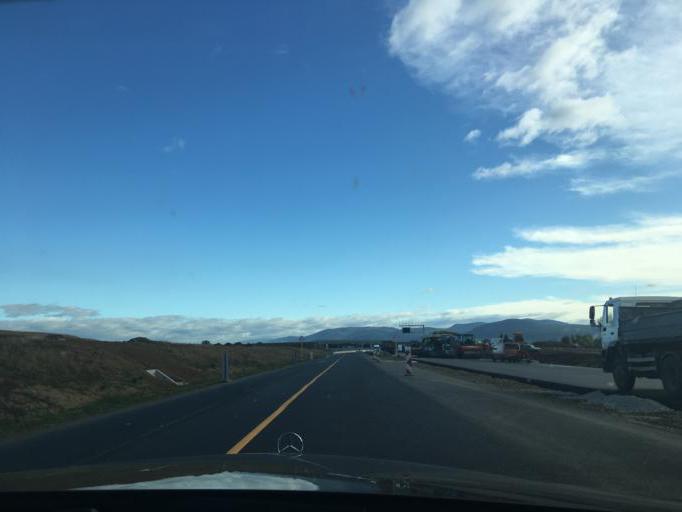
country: HU
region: Borsod-Abauj-Zemplen
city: Gonc
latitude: 48.5227
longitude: 21.2427
